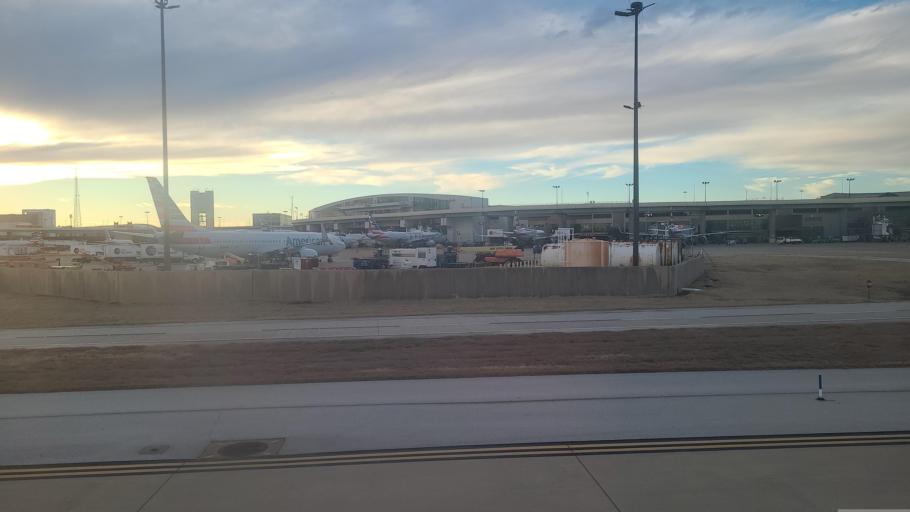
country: US
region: Texas
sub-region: Tarrant County
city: Grapevine
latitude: 32.9025
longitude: -97.0331
